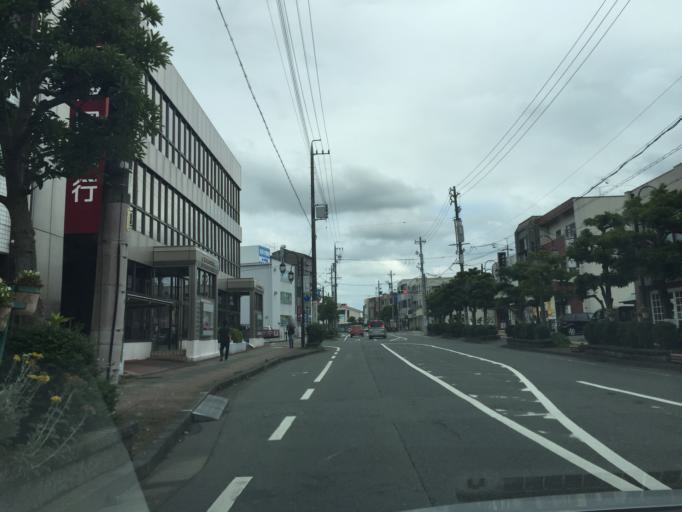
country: JP
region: Shizuoka
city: Fukuroi
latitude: 34.7437
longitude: 137.9245
